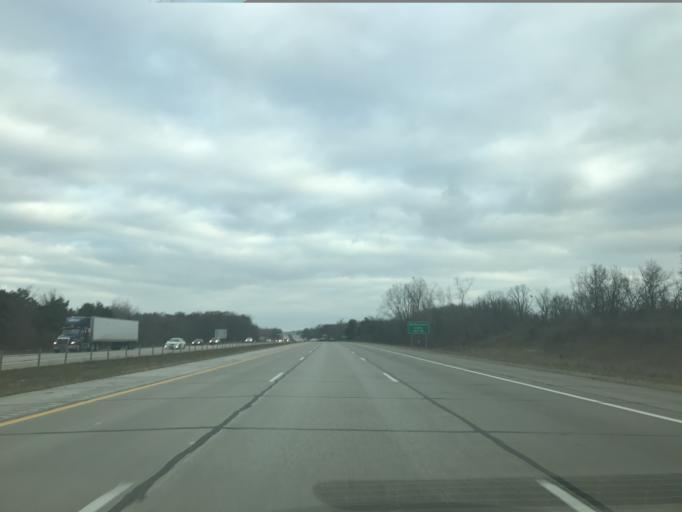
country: US
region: Michigan
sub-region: Eaton County
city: Waverly
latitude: 42.7581
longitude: -84.6674
